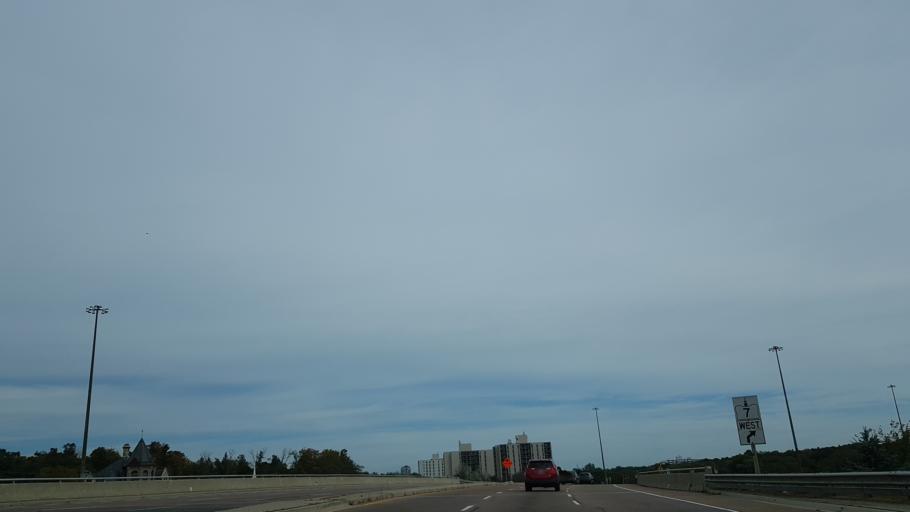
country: CA
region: Ontario
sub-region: Wellington County
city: Guelph
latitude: 43.5265
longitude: -80.2653
